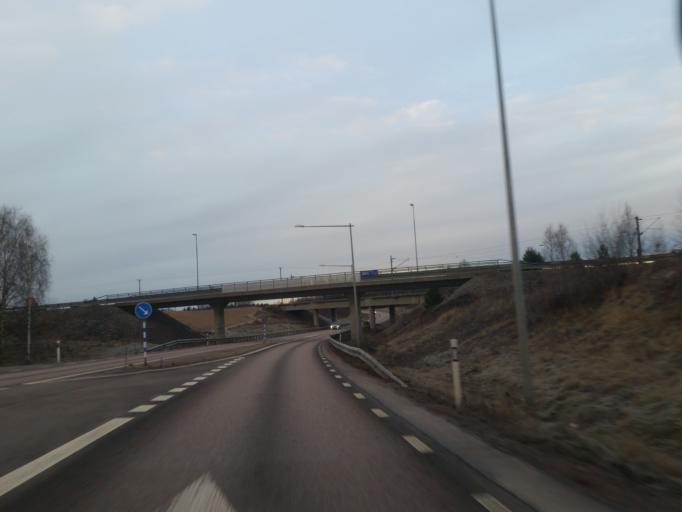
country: SE
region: Dalarna
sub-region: Leksand Municipality
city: Smedby
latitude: 60.6990
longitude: 15.0542
